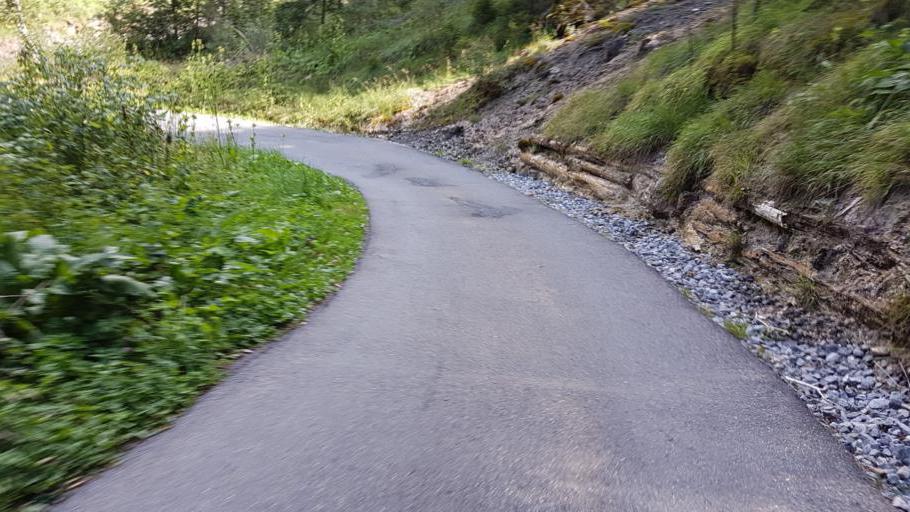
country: CH
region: Bern
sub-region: Frutigen-Niedersimmental District
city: Adelboden
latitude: 46.4901
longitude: 7.5812
